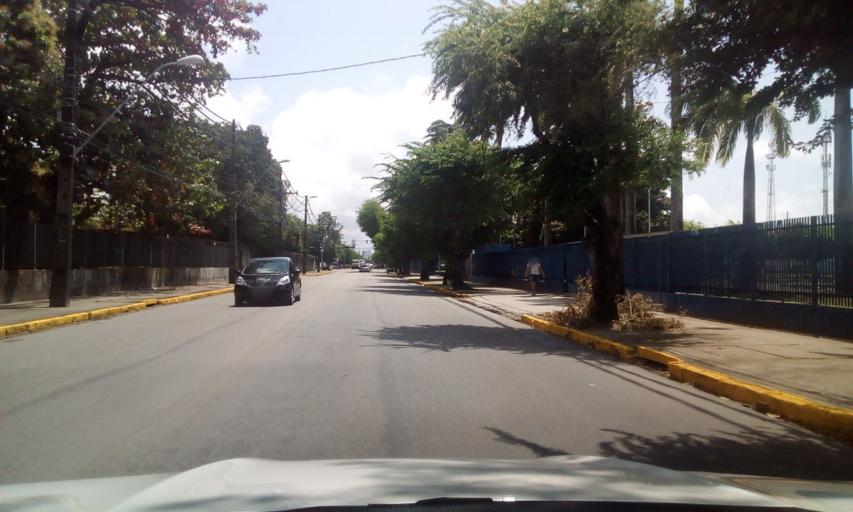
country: BR
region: Pernambuco
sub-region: Recife
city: Recife
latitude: -8.0621
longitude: -34.9263
